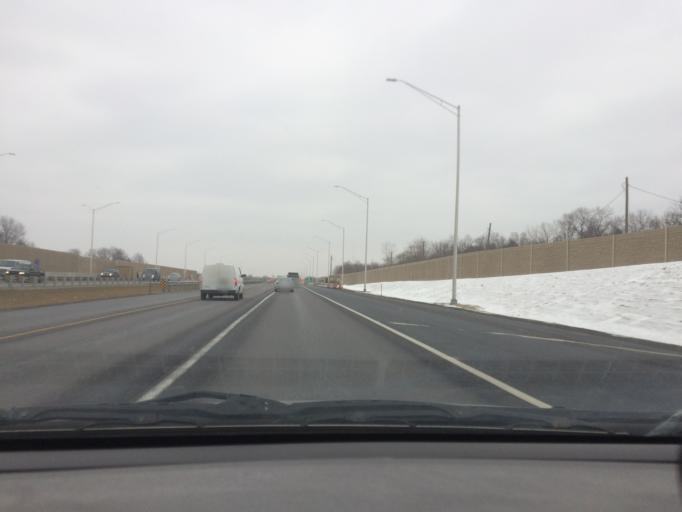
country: US
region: Illinois
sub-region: DuPage County
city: Roselle
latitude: 41.9920
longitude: -88.0606
